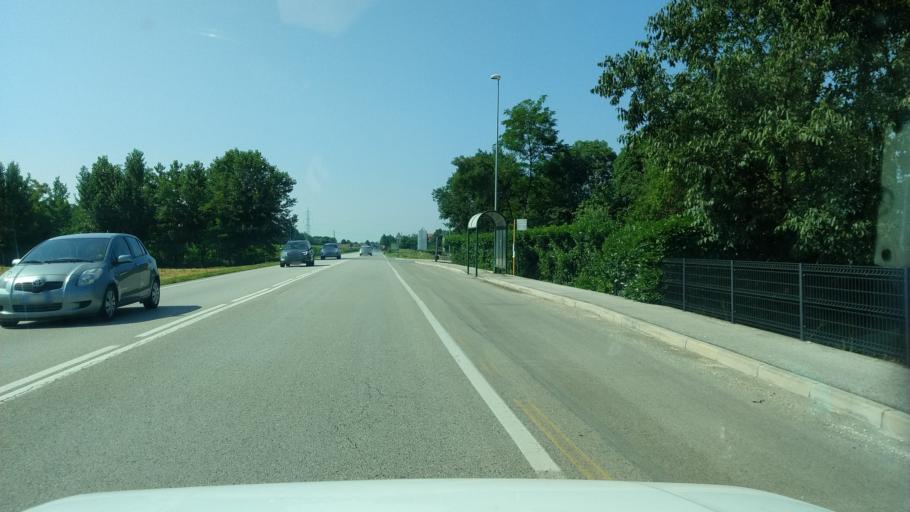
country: IT
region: Veneto
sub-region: Provincia di Vicenza
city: Schiavon
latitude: 45.6750
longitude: 11.6373
